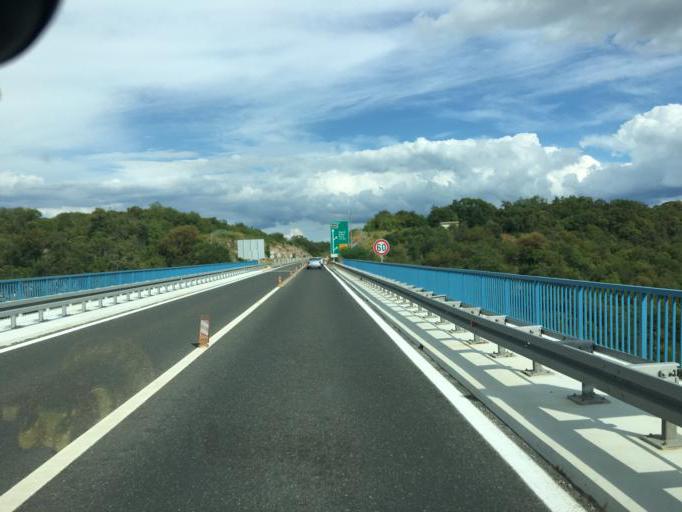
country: HR
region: Istarska
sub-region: Grad Rovinj
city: Rovinj
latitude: 45.1202
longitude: 13.8028
